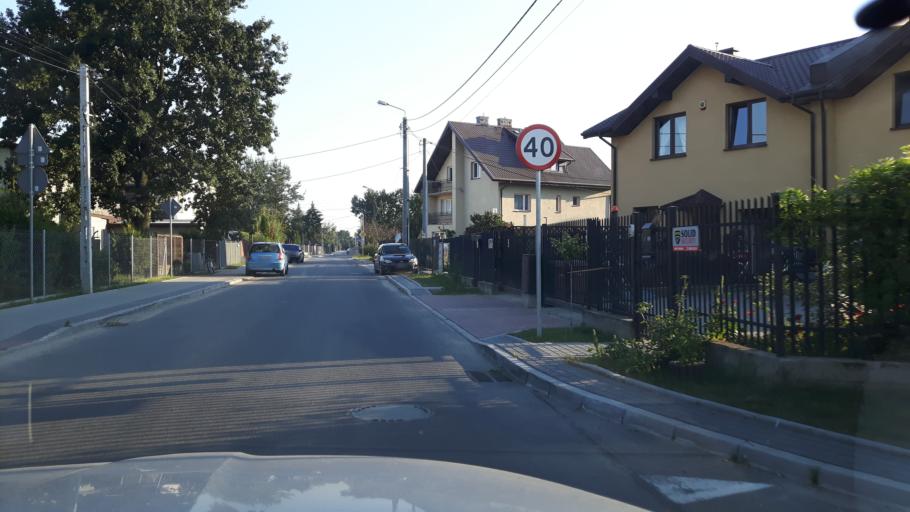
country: PL
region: Masovian Voivodeship
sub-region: Powiat wolominski
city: Kobylka
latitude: 52.3240
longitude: 21.1960
